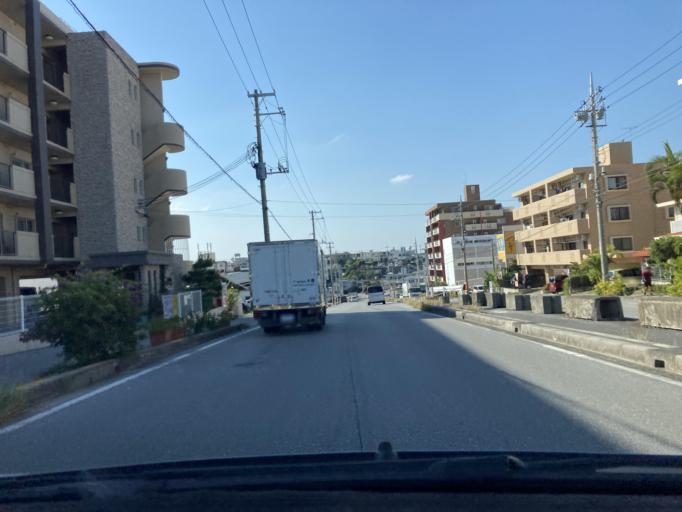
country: JP
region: Okinawa
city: Ginowan
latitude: 26.2362
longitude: 127.7234
